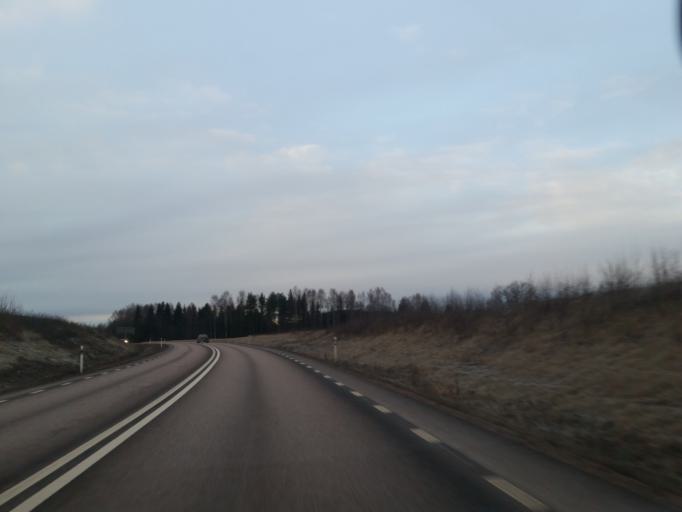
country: SE
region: Dalarna
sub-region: Leksand Municipality
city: Smedby
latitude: 60.7014
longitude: 15.0528
